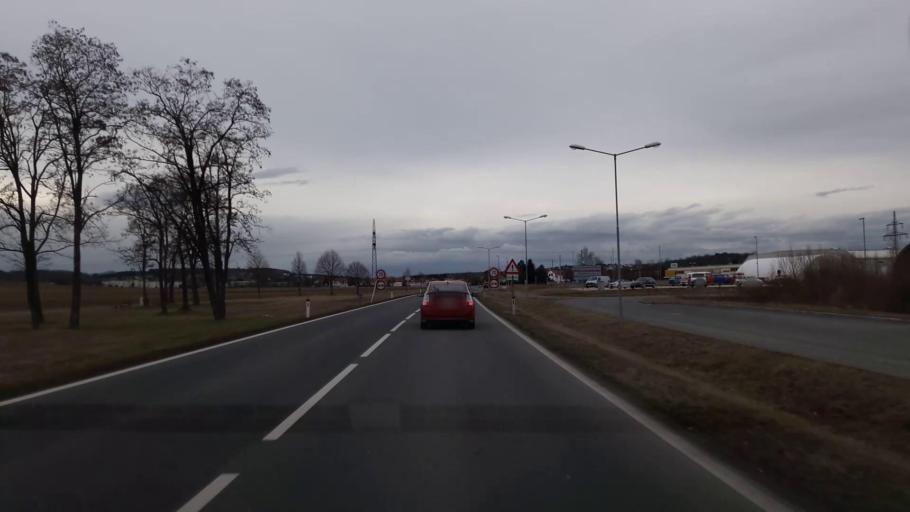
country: AT
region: Burgenland
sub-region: Politischer Bezirk Oberpullendorf
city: Oberpullendorf
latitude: 47.4858
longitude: 16.5238
